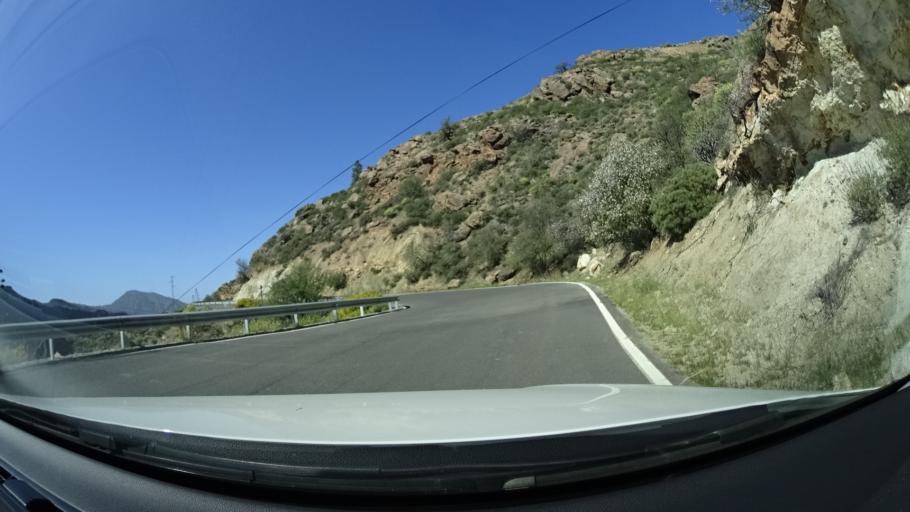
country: ES
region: Canary Islands
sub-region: Provincia de Las Palmas
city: Tejeda
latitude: 27.9881
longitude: -15.6365
